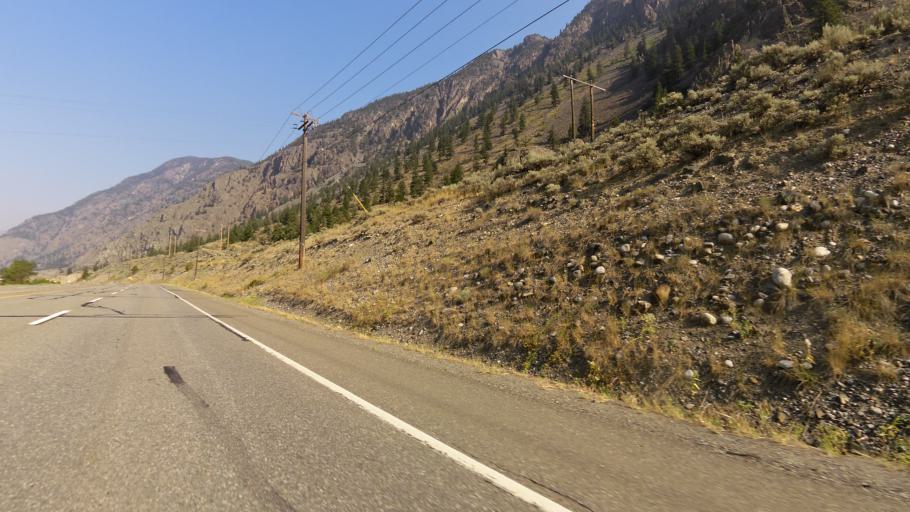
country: CA
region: British Columbia
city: Oliver
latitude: 49.2114
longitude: -119.8968
